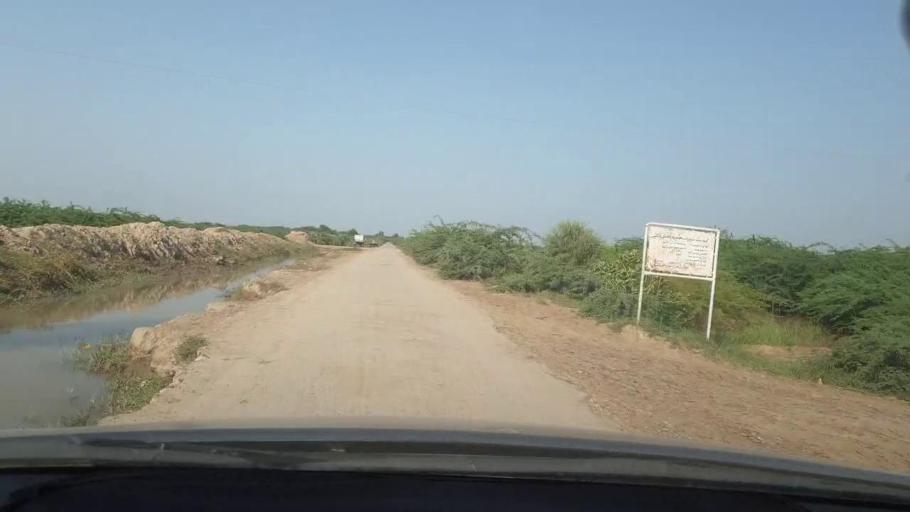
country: PK
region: Sindh
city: Naukot
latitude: 24.7725
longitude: 69.2581
